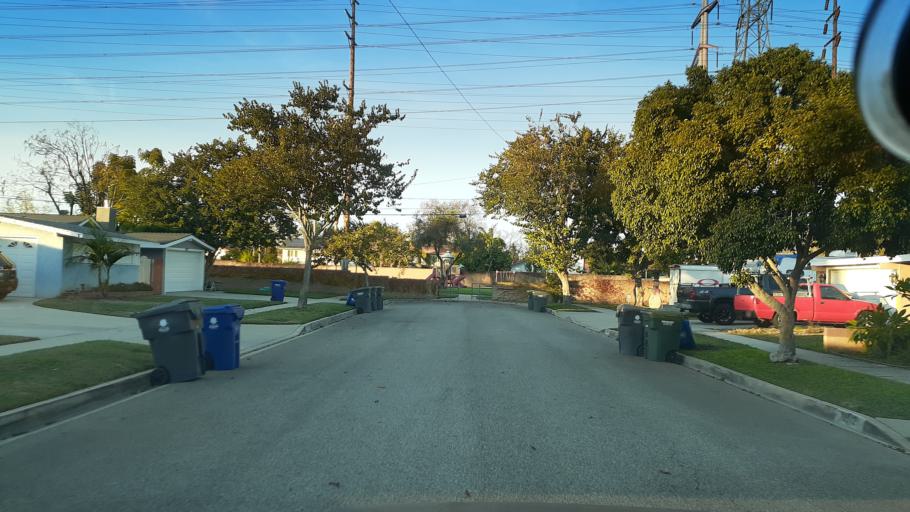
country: US
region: California
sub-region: Los Angeles County
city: Artesia
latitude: 33.8492
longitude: -118.0834
